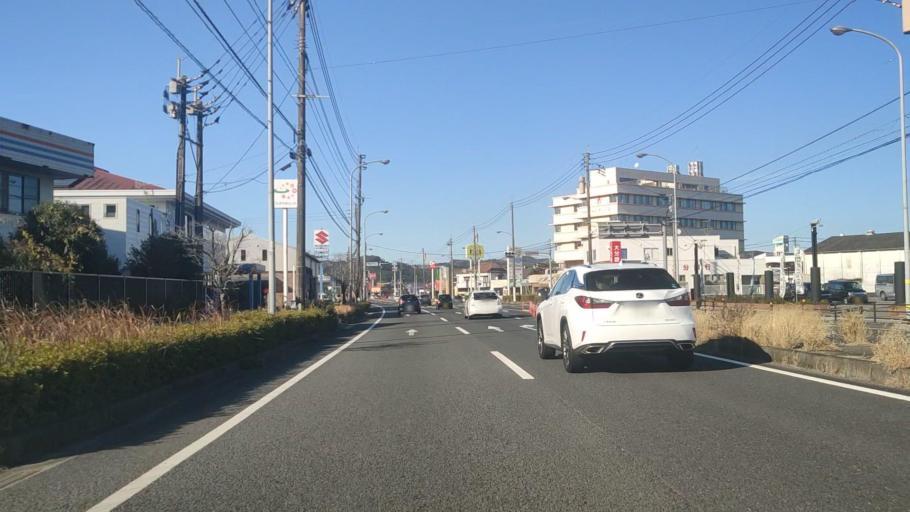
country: JP
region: Oita
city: Oita
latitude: 33.1531
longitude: 131.6560
